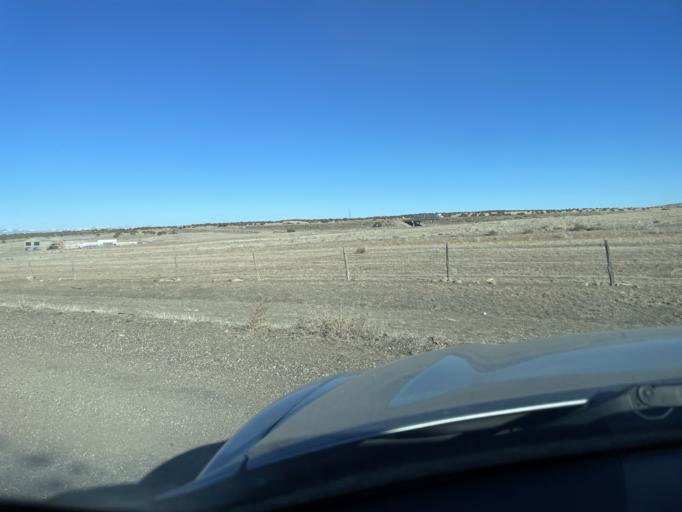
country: US
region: Colorado
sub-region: Mesa County
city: Loma
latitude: 39.1744
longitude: -109.1332
